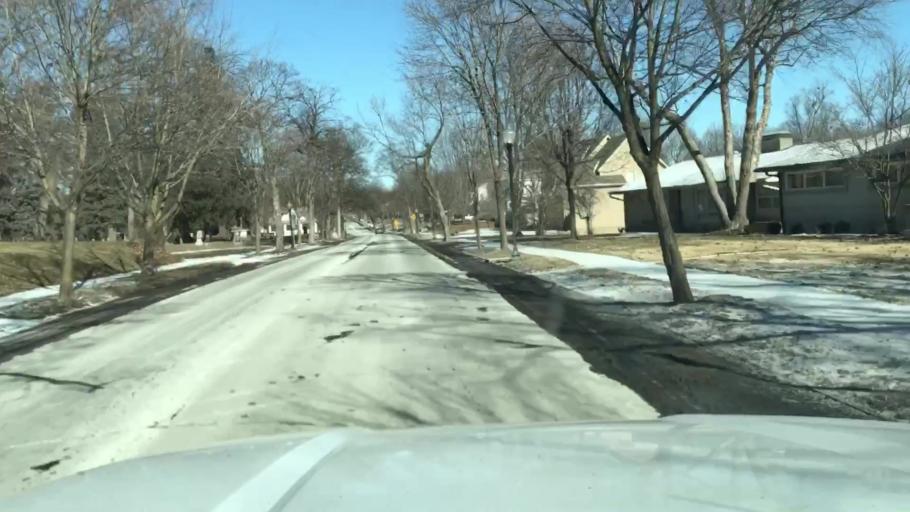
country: US
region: Missouri
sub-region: Buchanan County
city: Saint Joseph
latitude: 39.7862
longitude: -94.8221
